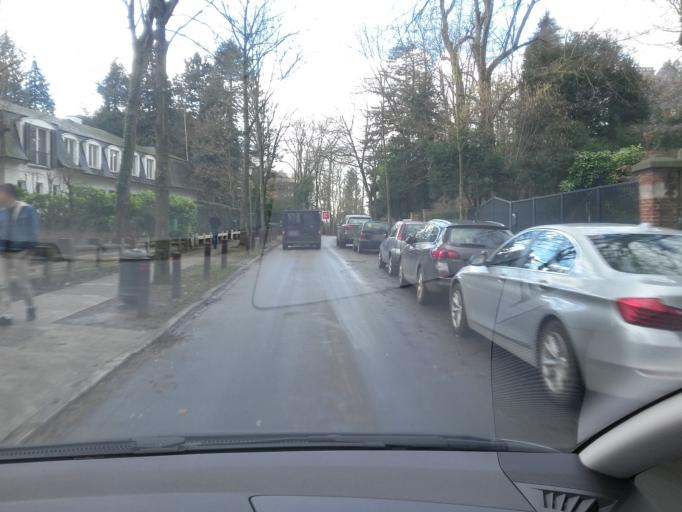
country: BE
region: Flanders
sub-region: Provincie Vlaams-Brabant
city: Linkebeek
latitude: 50.7986
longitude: 4.3748
